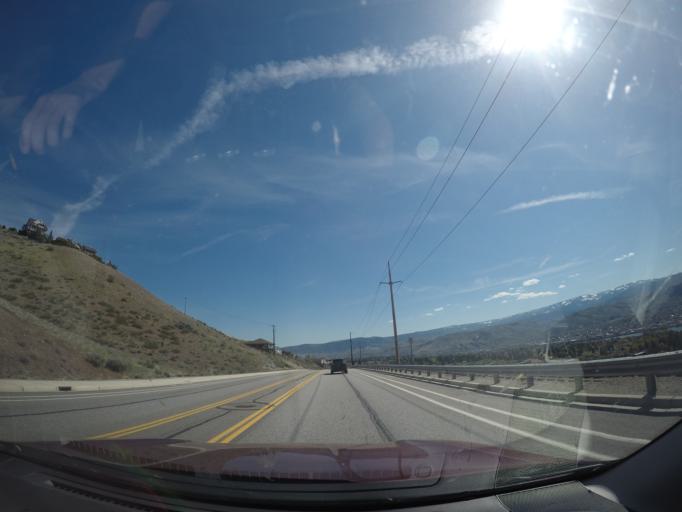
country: US
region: Washington
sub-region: Douglas County
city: East Wenatchee Bench
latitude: 47.4436
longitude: -120.2843
